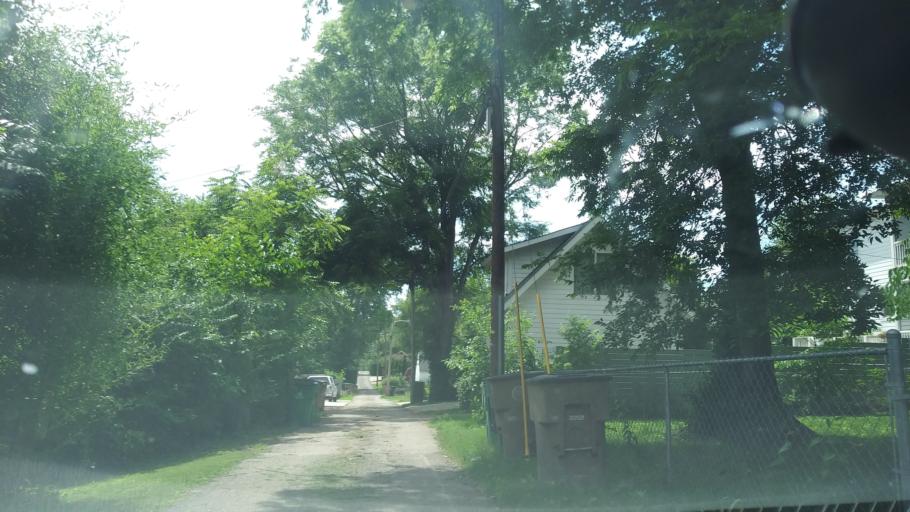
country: US
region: Tennessee
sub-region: Davidson County
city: Belle Meade
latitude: 36.1424
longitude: -86.8331
